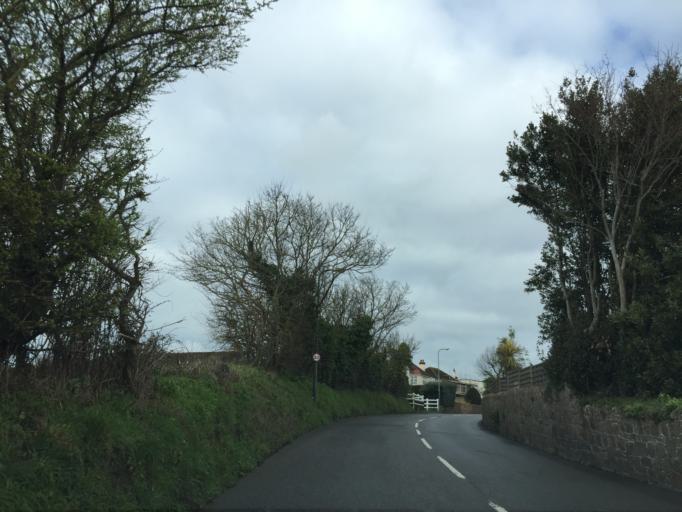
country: JE
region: St Helier
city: Saint Helier
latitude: 49.2046
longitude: -2.1412
